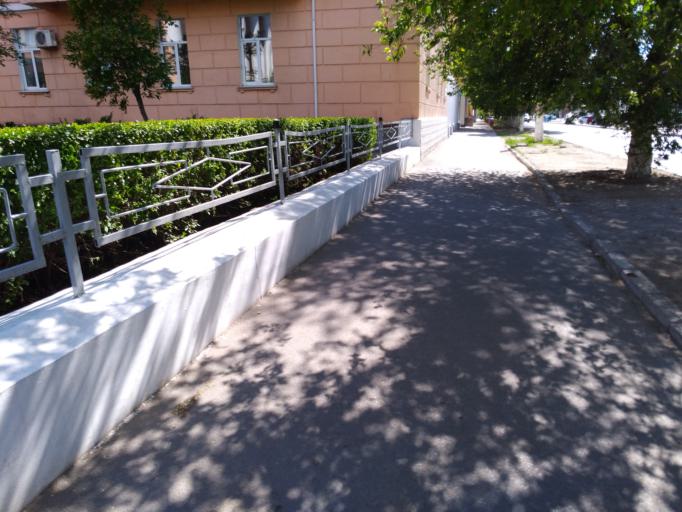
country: RU
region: Volgograd
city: Volgograd
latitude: 48.7160
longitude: 44.5240
